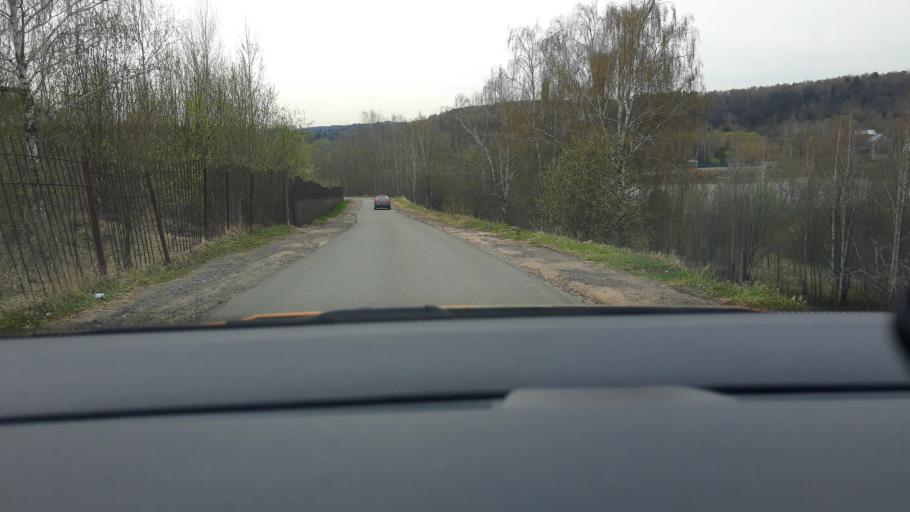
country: RU
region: Moskovskaya
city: Novopodrezkovo
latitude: 55.9260
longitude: 37.3494
